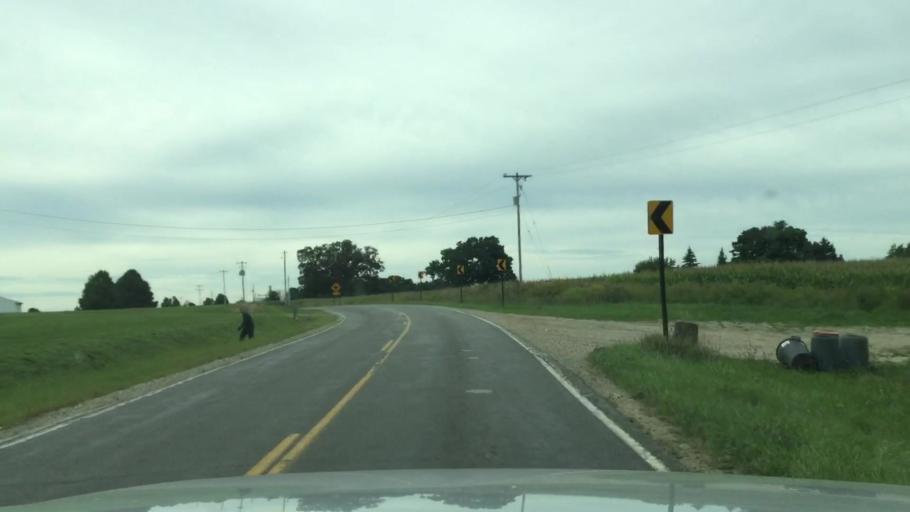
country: US
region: Michigan
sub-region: Shiawassee County
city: Durand
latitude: 42.9528
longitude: -83.9888
